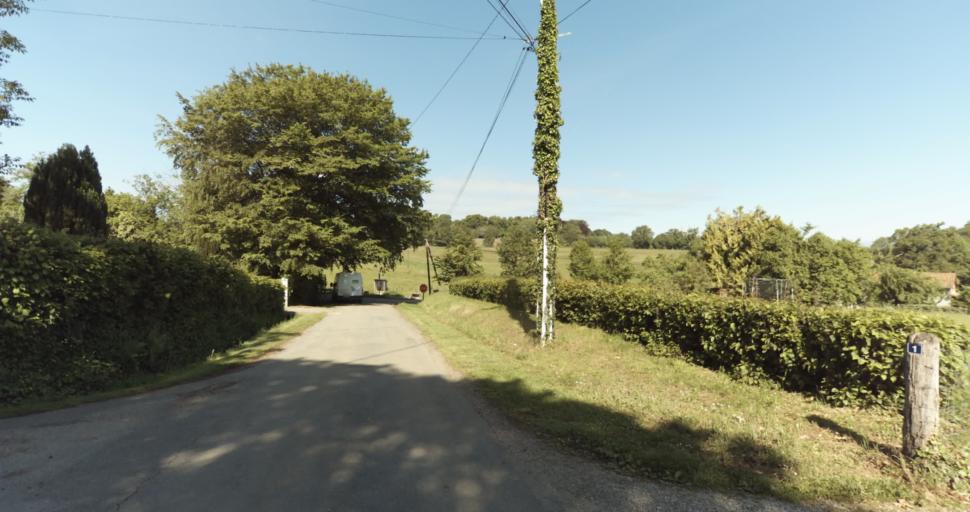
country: FR
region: Limousin
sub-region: Departement de la Haute-Vienne
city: Solignac
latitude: 45.7227
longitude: 1.2697
